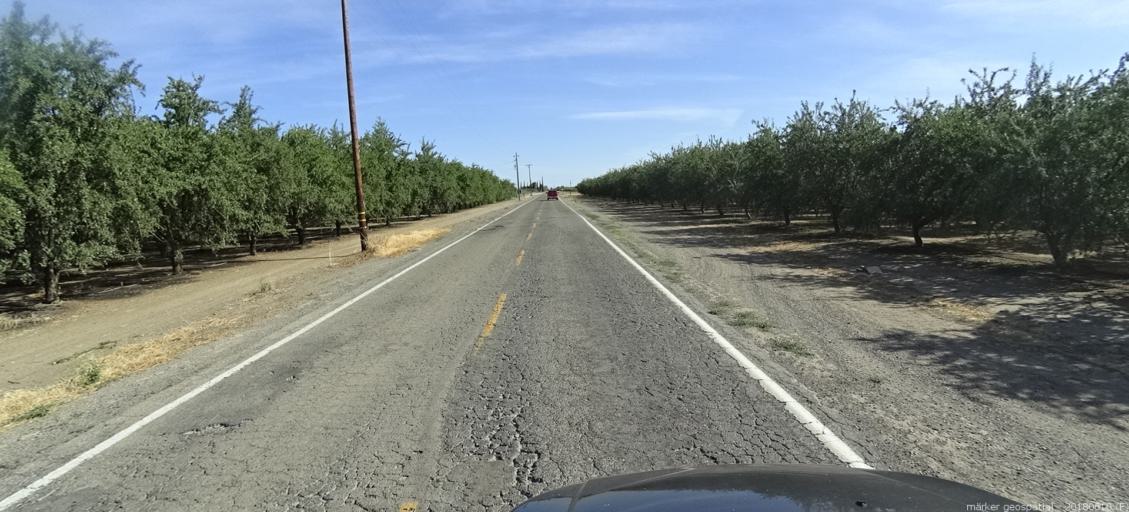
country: US
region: California
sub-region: Madera County
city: Chowchilla
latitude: 37.0637
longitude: -120.2568
